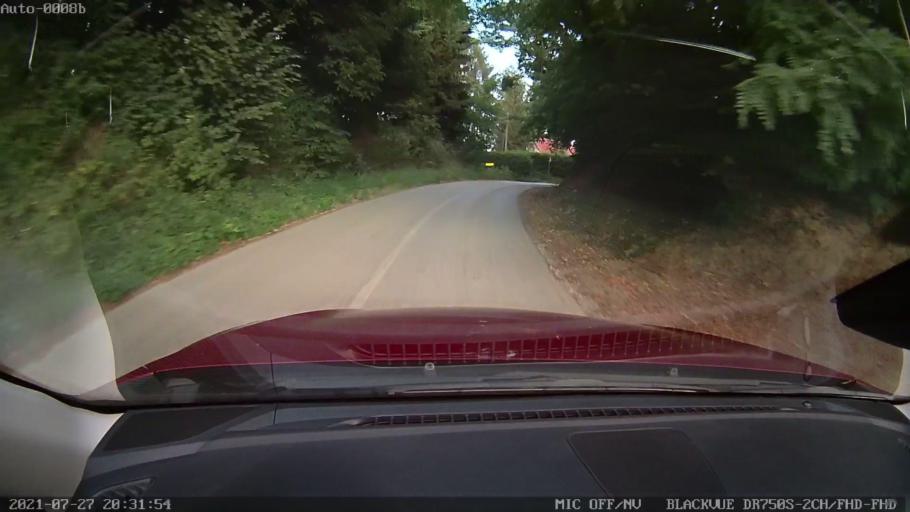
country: HR
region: Varazdinska
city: Jalzabet
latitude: 46.2459
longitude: 16.4742
